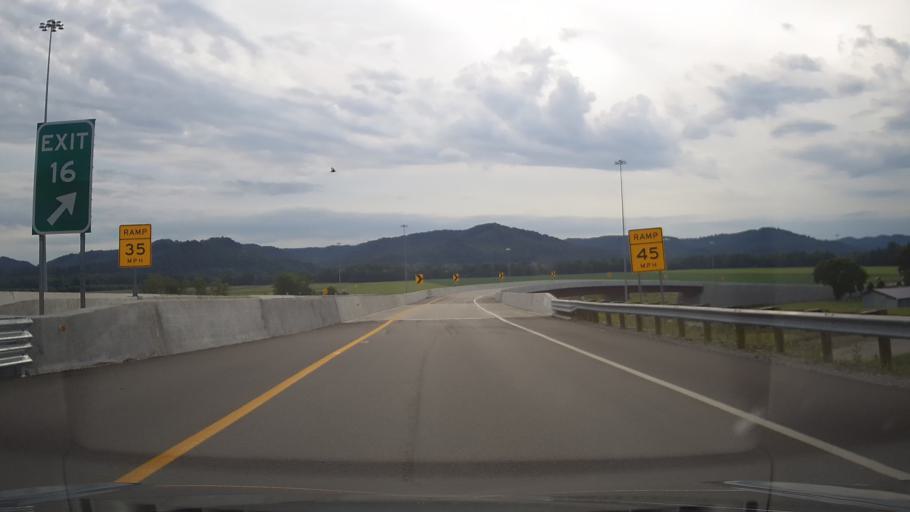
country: US
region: Ohio
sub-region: Scioto County
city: Lucasville
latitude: 38.8923
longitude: -82.9972
